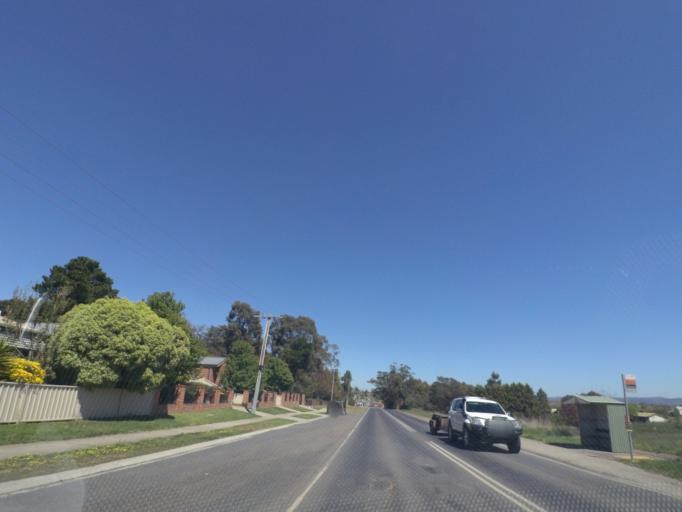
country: AU
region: Victoria
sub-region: Whittlesea
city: Whittlesea
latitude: -37.2895
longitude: 144.9557
